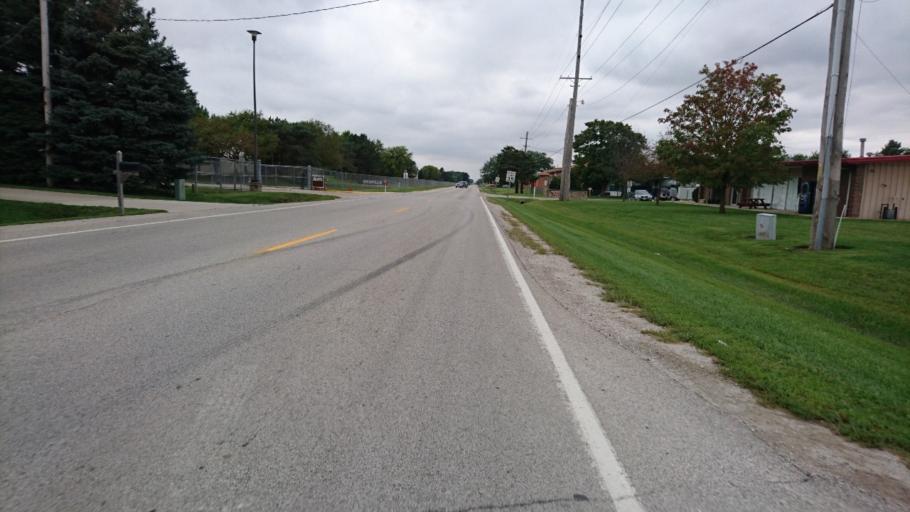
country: US
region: Illinois
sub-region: Livingston County
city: Pontiac
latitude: 40.8882
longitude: -88.6498
